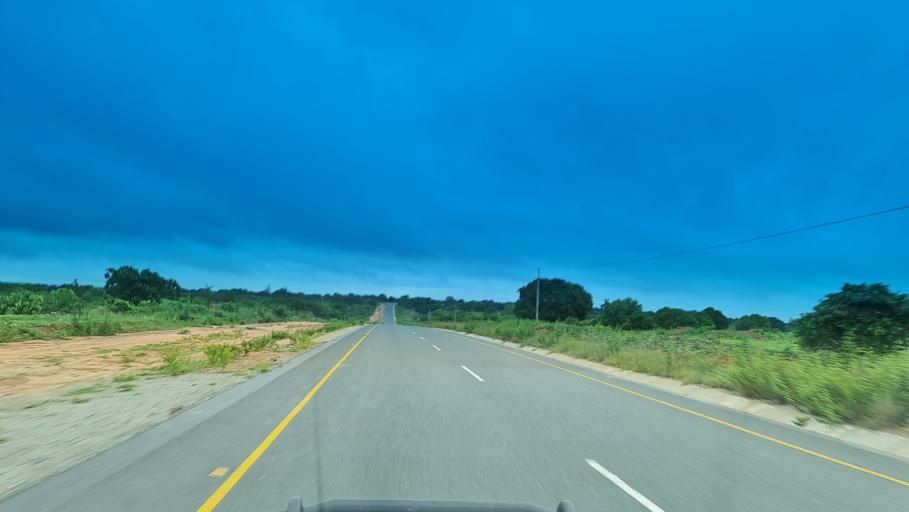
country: MZ
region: Nampula
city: Nampula
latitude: -15.6081
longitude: 39.3290
